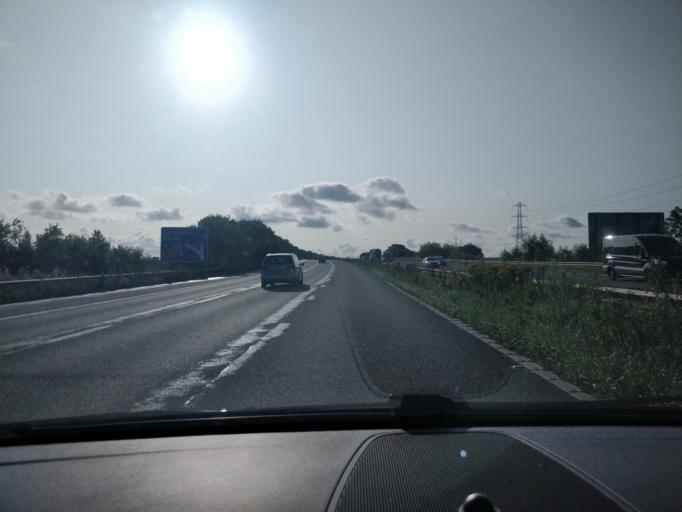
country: GB
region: England
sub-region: Sefton
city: Melling
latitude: 53.4851
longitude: -2.9265
